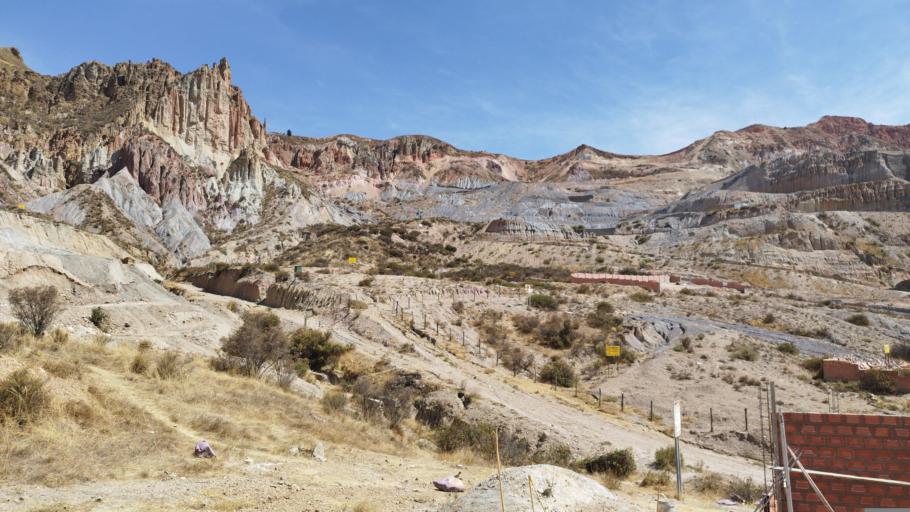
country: BO
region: La Paz
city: La Paz
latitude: -16.5516
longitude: -68.0636
